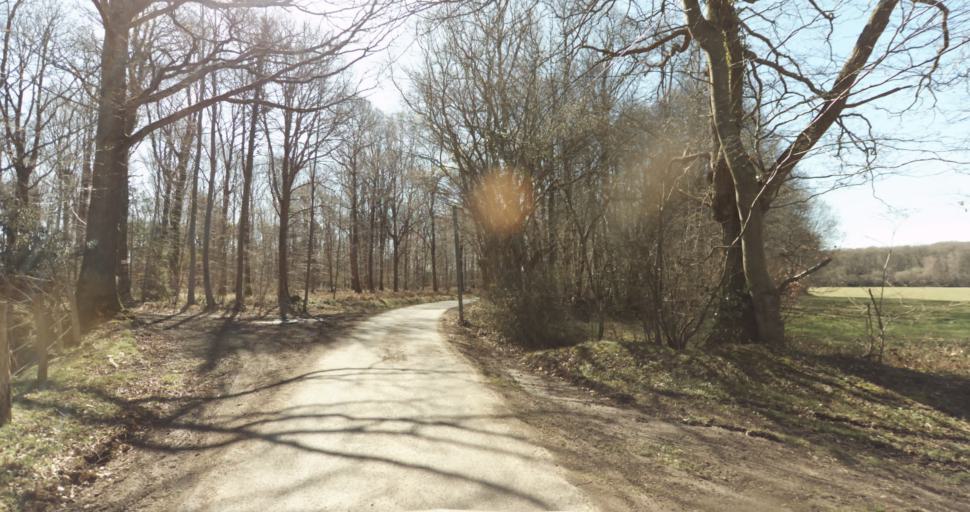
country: FR
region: Lower Normandy
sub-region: Departement du Calvados
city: Livarot
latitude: 48.9737
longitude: 0.0950
